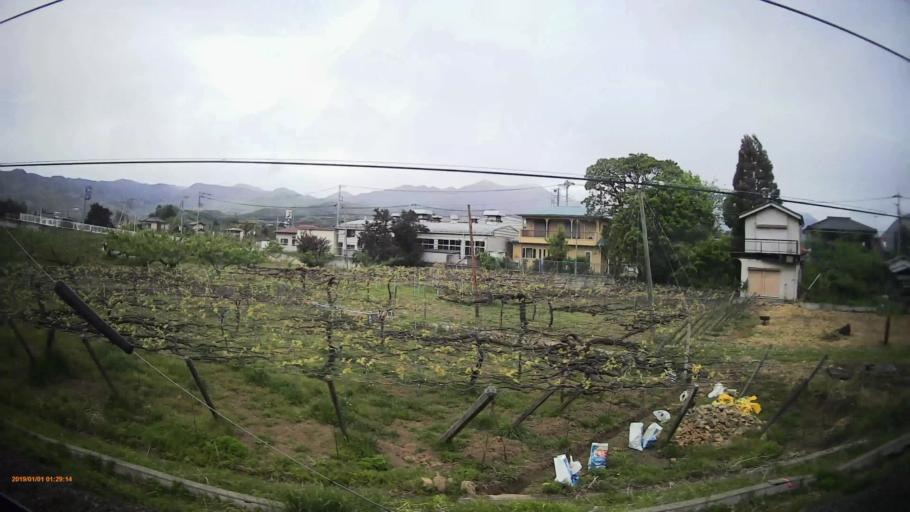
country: JP
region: Yamanashi
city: Enzan
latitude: 35.7006
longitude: 138.7143
